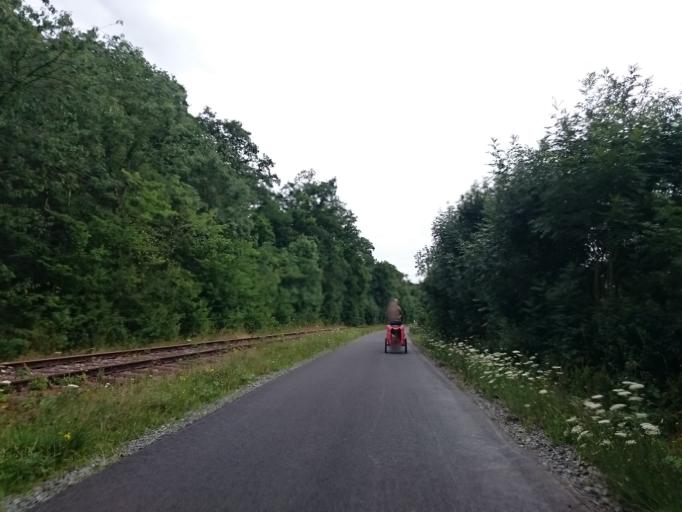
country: FR
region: Lower Normandy
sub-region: Departement du Calvados
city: Clinchamps-sur-Orne
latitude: 49.0735
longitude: -0.4304
